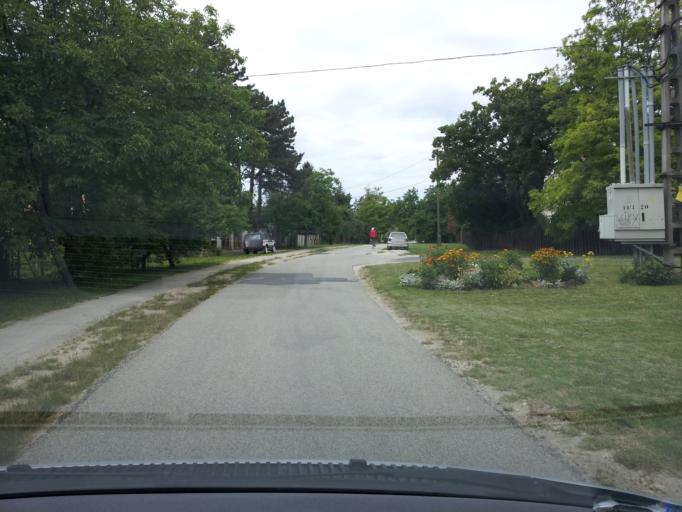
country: HU
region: Veszprem
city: Balatonkenese
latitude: 47.0205
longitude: 18.1572
